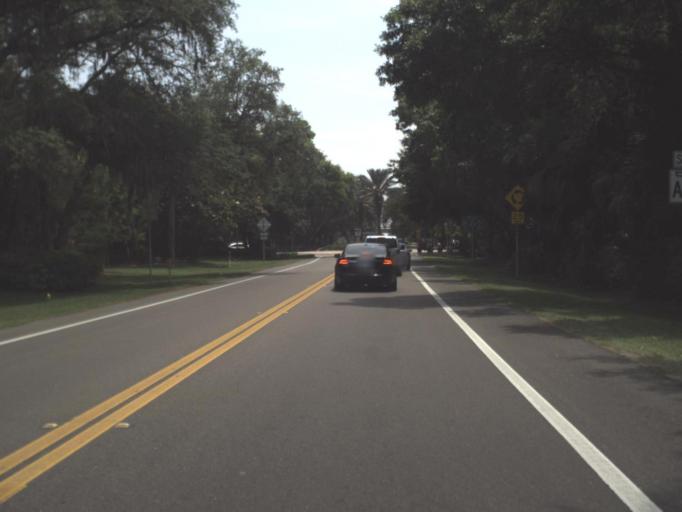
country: US
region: Florida
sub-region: Nassau County
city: Fernandina Beach
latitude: 30.5566
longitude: -81.4499
